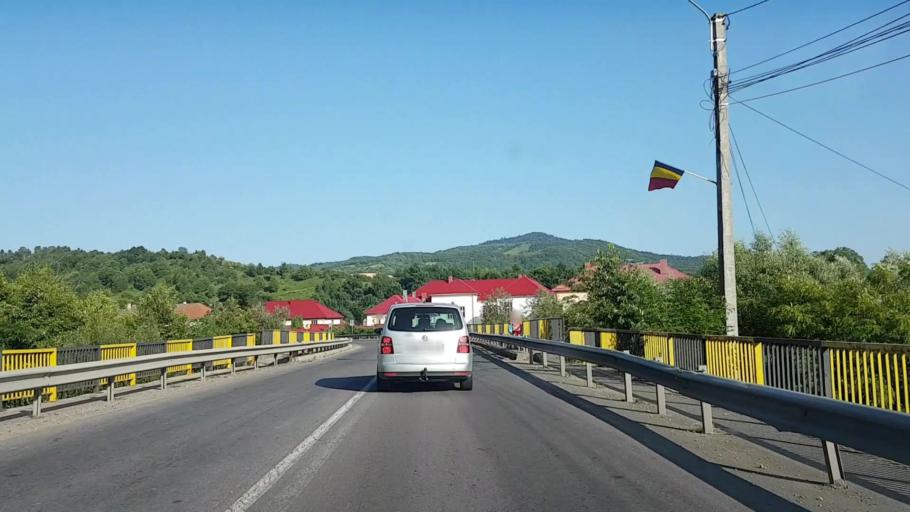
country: RO
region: Bistrita-Nasaud
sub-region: Comuna Josenii Bargaului
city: Josenii Bargaului
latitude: 47.2124
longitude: 24.6762
